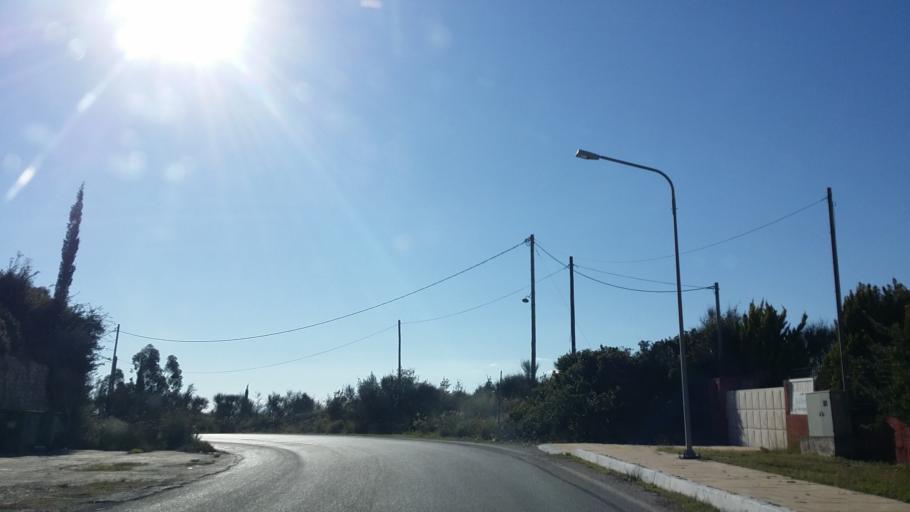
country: GR
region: West Greece
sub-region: Nomos Aitolias kai Akarnanias
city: Palairos
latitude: 38.7686
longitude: 20.8812
